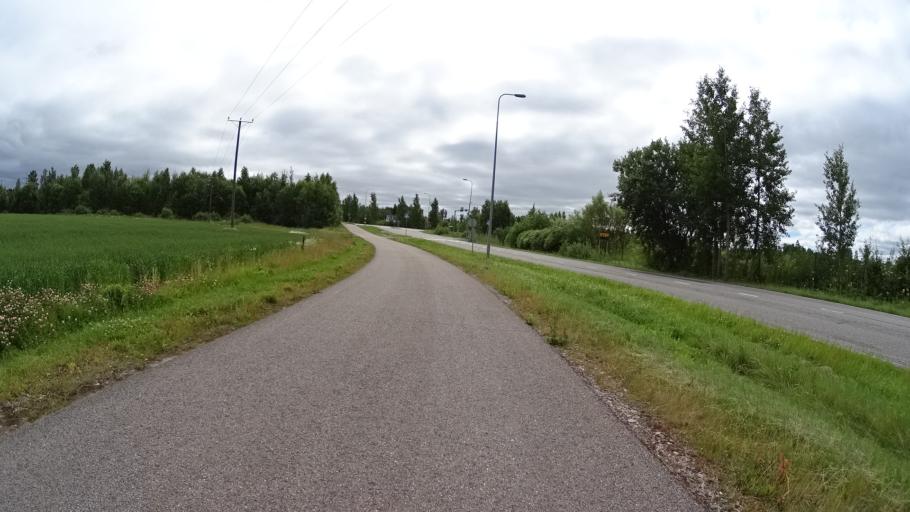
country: FI
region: Uusimaa
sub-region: Helsinki
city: Kauniainen
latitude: 60.2530
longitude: 24.7077
